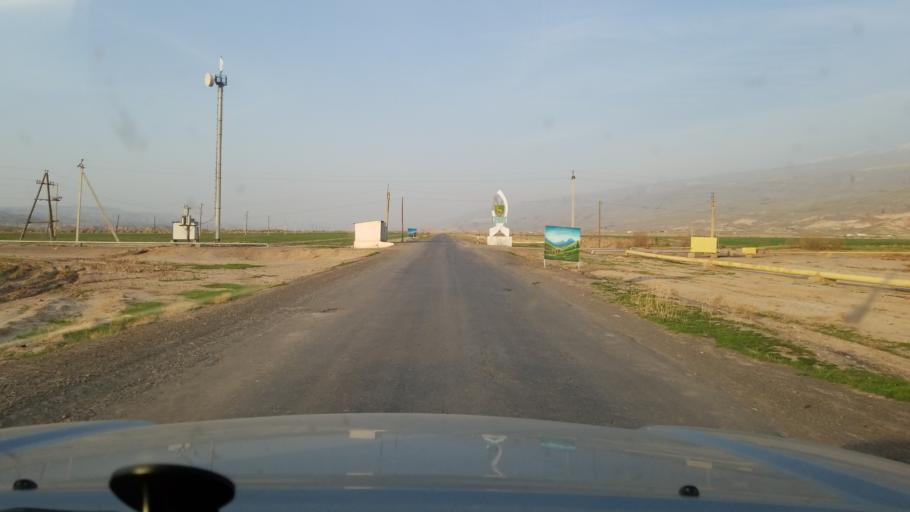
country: TM
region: Lebap
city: Gowurdak
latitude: 37.7619
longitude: 66.3596
